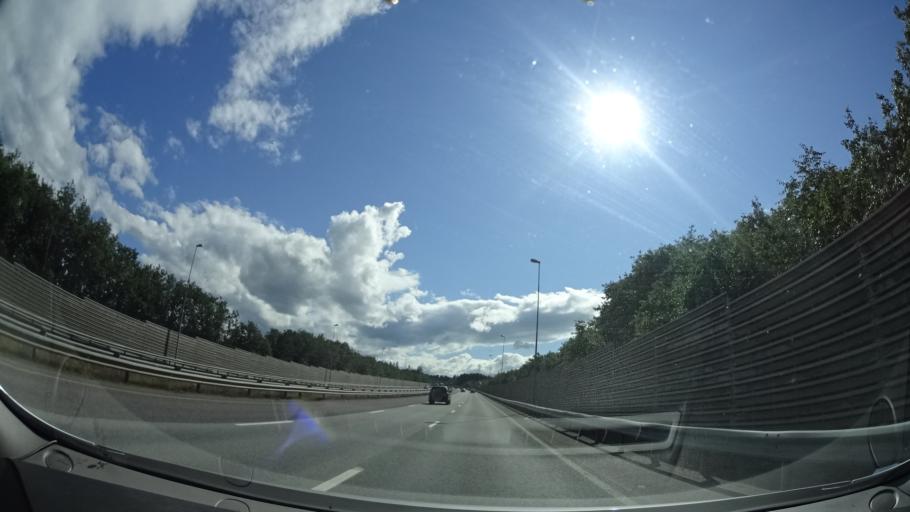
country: NO
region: Sor-Trondelag
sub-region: Trondheim
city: Trondheim
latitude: 63.3888
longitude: 10.3805
